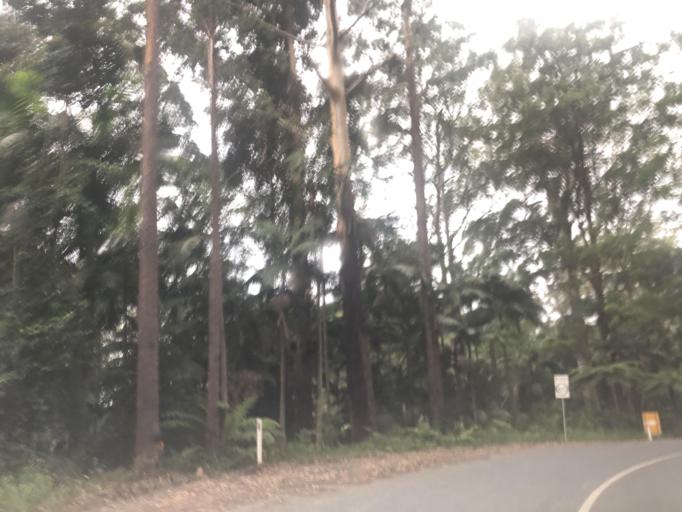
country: AU
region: New South Wales
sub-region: Coffs Harbour
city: Nana Glen
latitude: -30.2189
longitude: 152.9572
